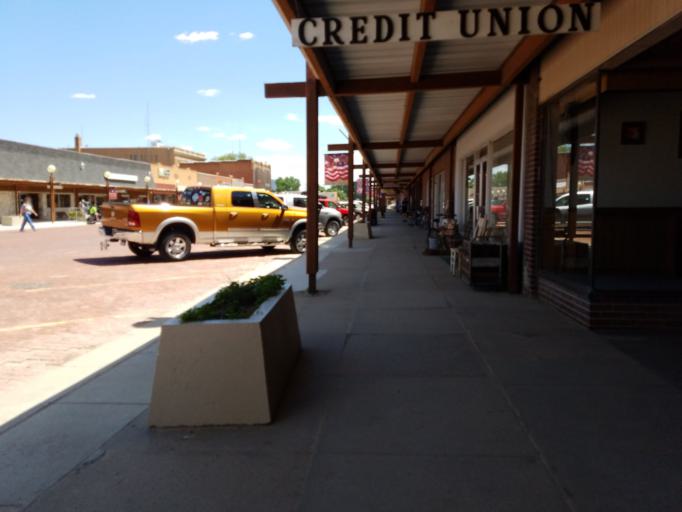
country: US
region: Kansas
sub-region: Decatur County
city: Oberlin
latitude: 39.8205
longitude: -100.5292
